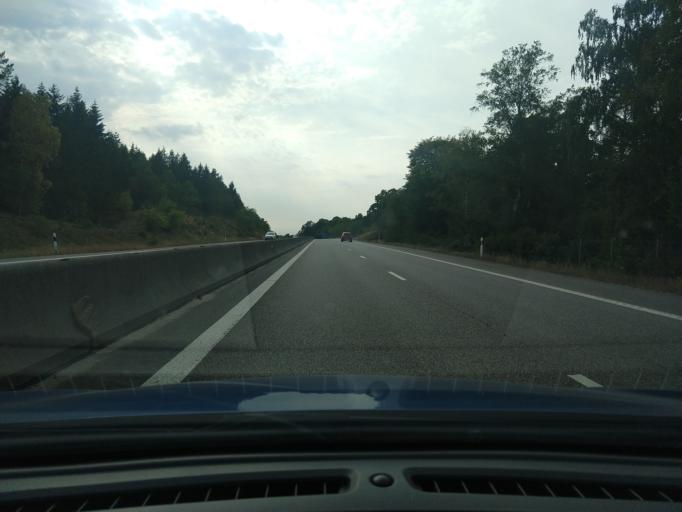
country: SE
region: Blekinge
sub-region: Karlskrona Kommun
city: Nattraby
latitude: 56.2099
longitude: 15.5564
